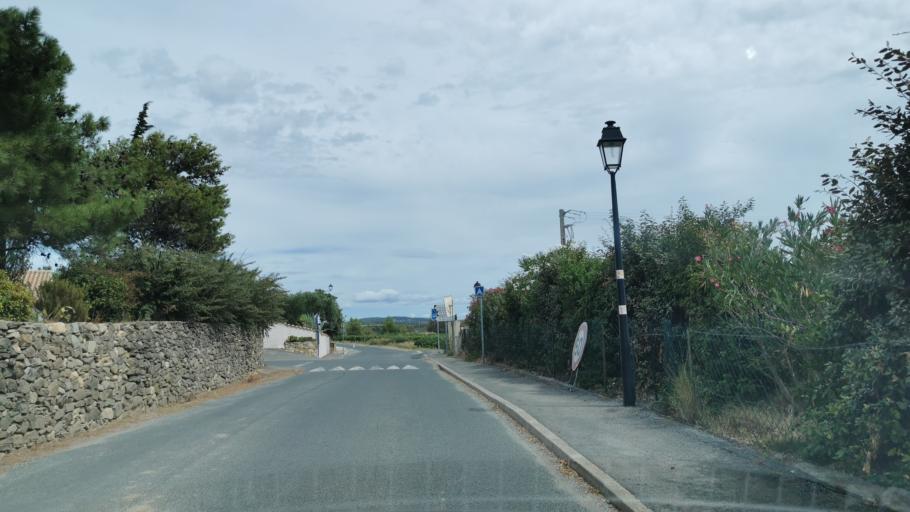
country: FR
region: Languedoc-Roussillon
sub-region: Departement de l'Aude
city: Ginestas
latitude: 43.2889
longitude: 2.8239
